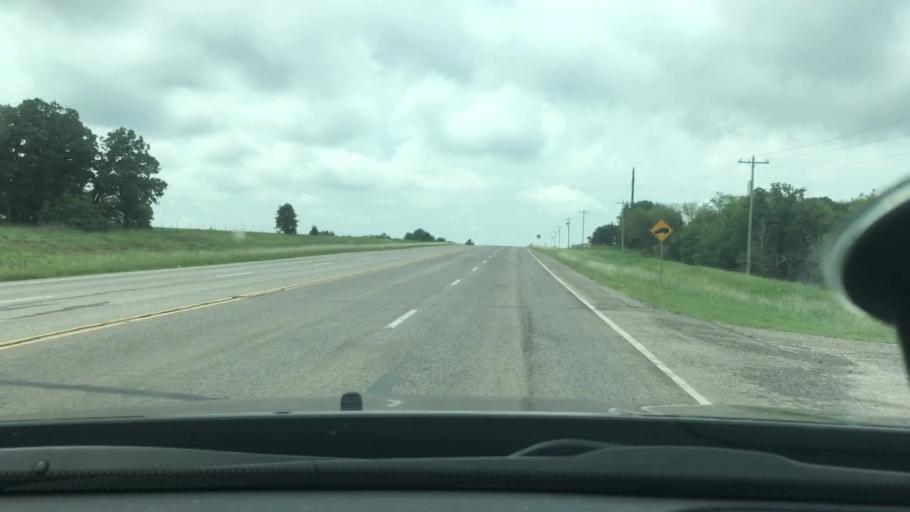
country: US
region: Oklahoma
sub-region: Carter County
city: Healdton
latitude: 34.1821
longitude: -97.4749
